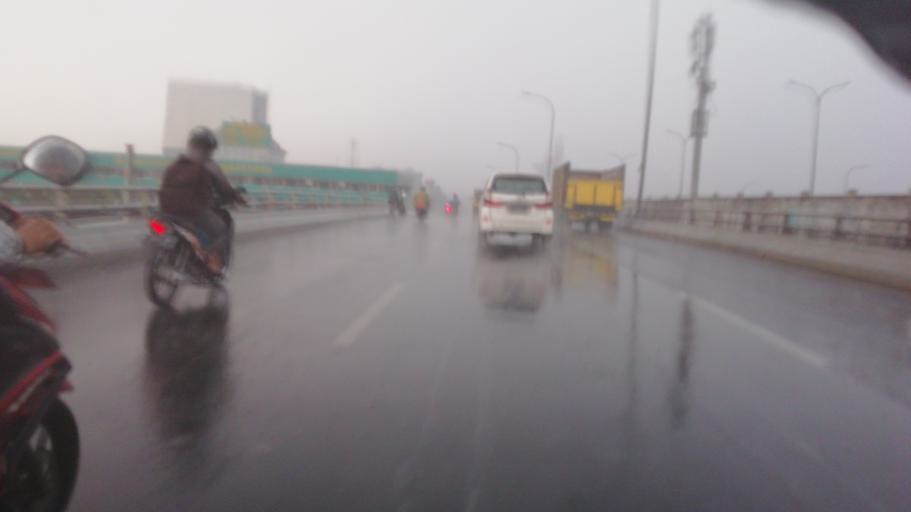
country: ID
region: Jakarta Raya
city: Jakarta
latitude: -6.3027
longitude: 106.8397
